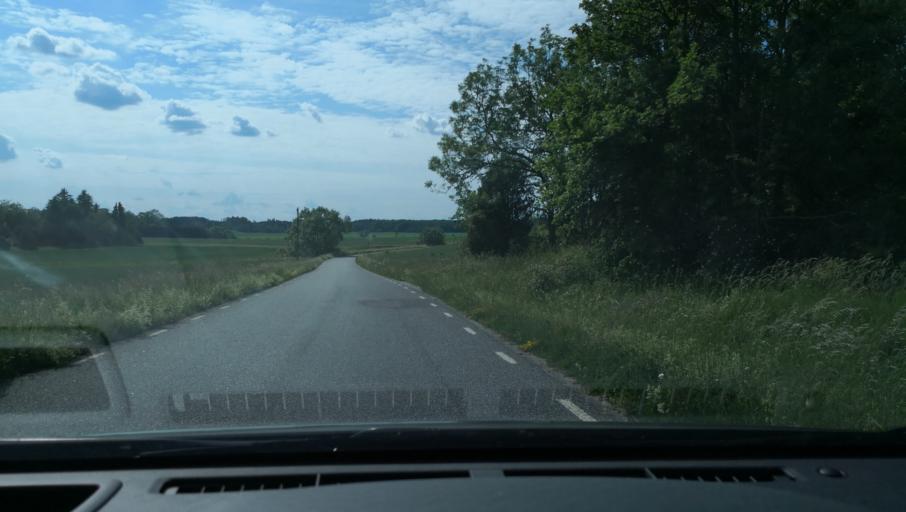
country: SE
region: Uppsala
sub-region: Enkopings Kommun
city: Orsundsbro
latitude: 59.8350
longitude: 17.3113
